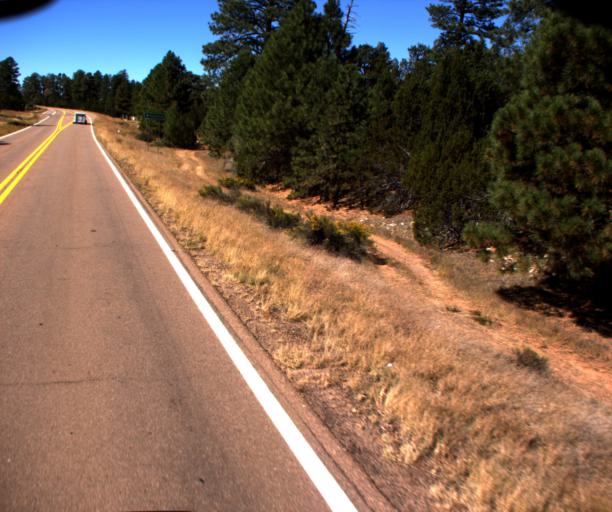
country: US
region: Arizona
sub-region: Navajo County
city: Heber-Overgaard
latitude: 34.4301
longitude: -110.5471
